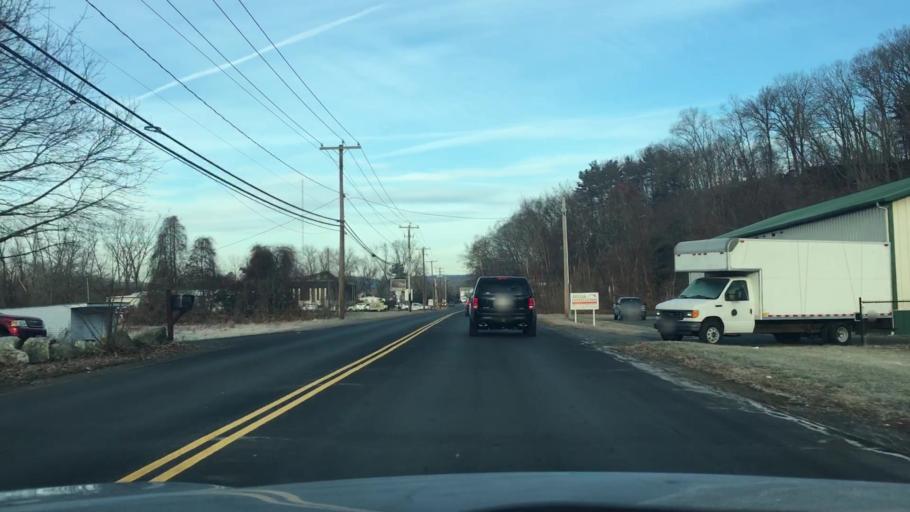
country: US
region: Massachusetts
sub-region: Hampden County
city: Westfield
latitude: 42.1224
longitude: -72.7181
